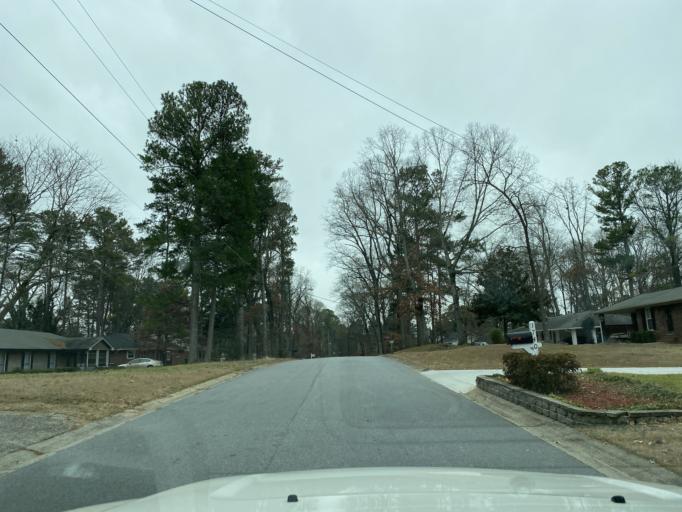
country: US
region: Georgia
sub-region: Cobb County
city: Fair Oaks
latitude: 33.9130
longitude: -84.5844
